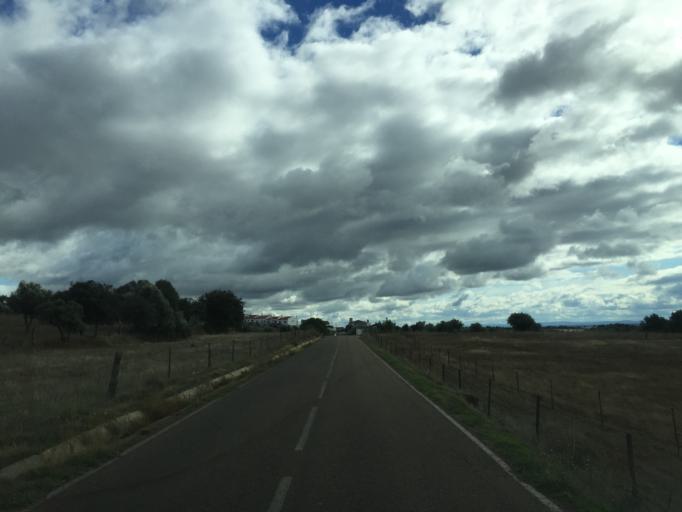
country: PT
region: Portalegre
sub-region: Alter do Chao
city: Alter do Chao
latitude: 39.2072
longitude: -7.6654
